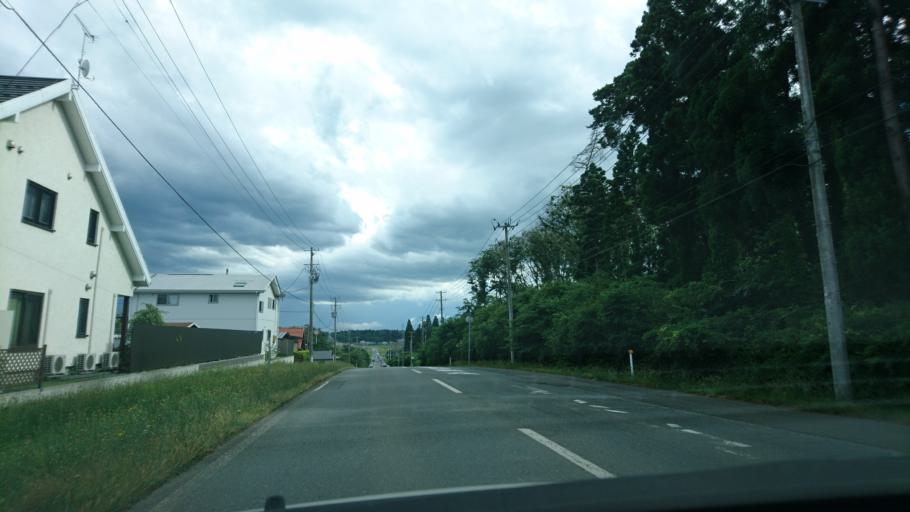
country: JP
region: Iwate
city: Kitakami
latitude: 39.3243
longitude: 141.1274
